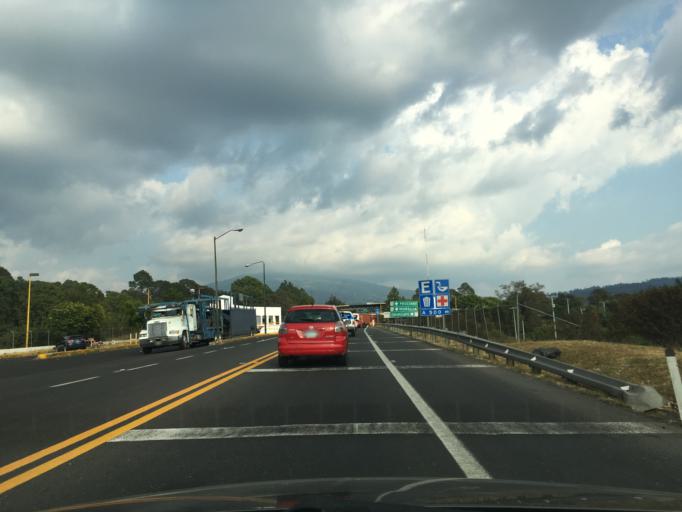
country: MX
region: Michoacan
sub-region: Ziracuaretiro
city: Patuan
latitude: 19.4408
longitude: -101.8845
